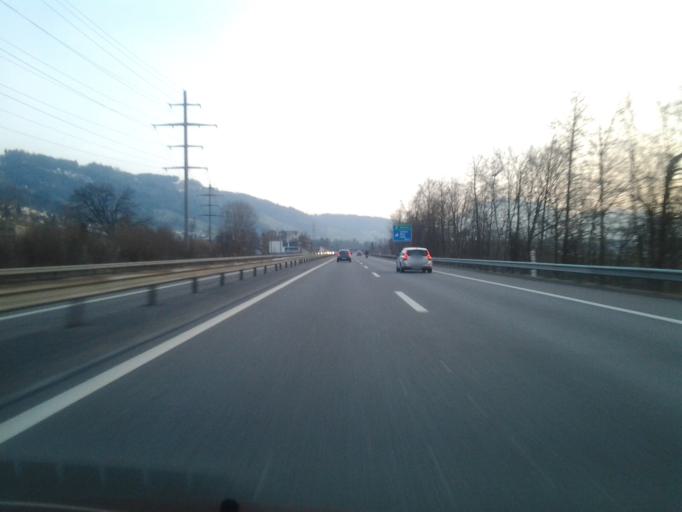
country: CH
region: Lucerne
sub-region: Lucerne-Land District
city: Root
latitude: 47.1320
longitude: 8.3977
